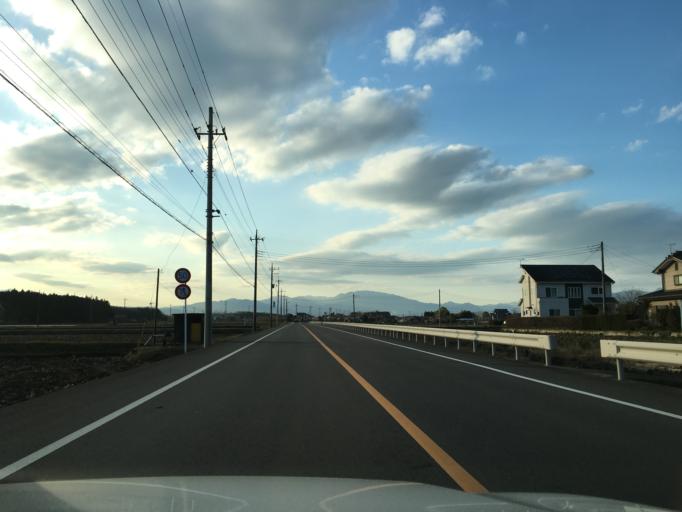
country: JP
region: Tochigi
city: Otawara
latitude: 36.8760
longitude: 140.0710
